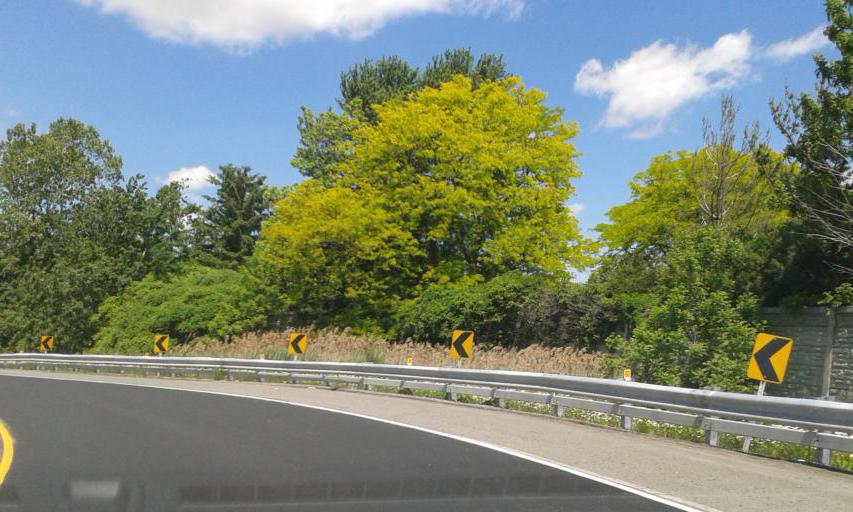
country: CA
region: Ontario
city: Niagara Falls
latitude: 43.1151
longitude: -79.1181
